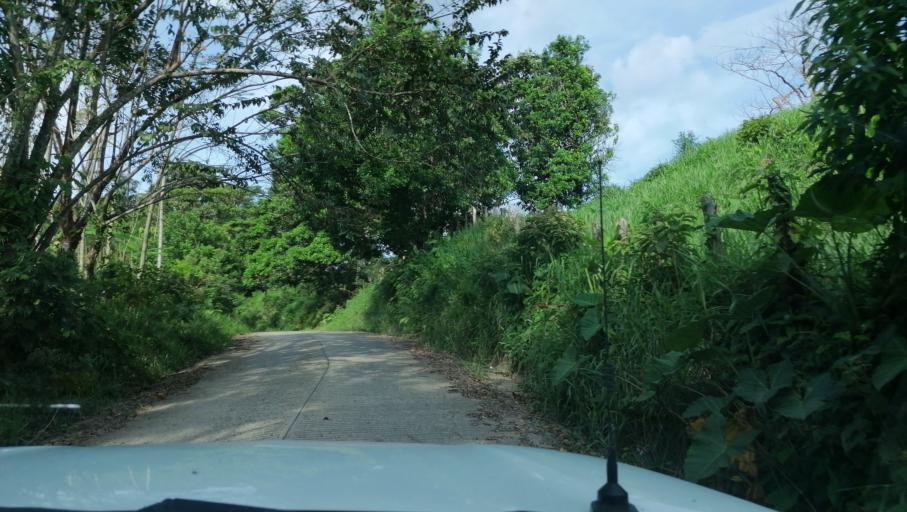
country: MX
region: Chiapas
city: Ostuacan
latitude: 17.4773
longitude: -93.2393
